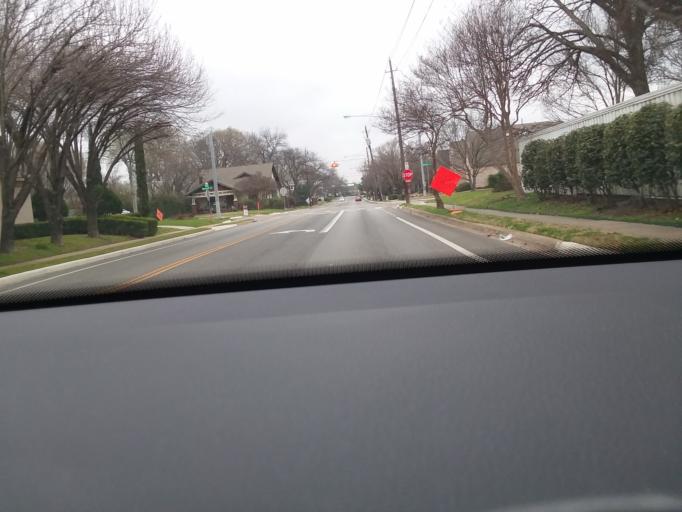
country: US
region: Texas
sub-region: Dallas County
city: Highland Park
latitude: 32.8179
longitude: -96.7681
